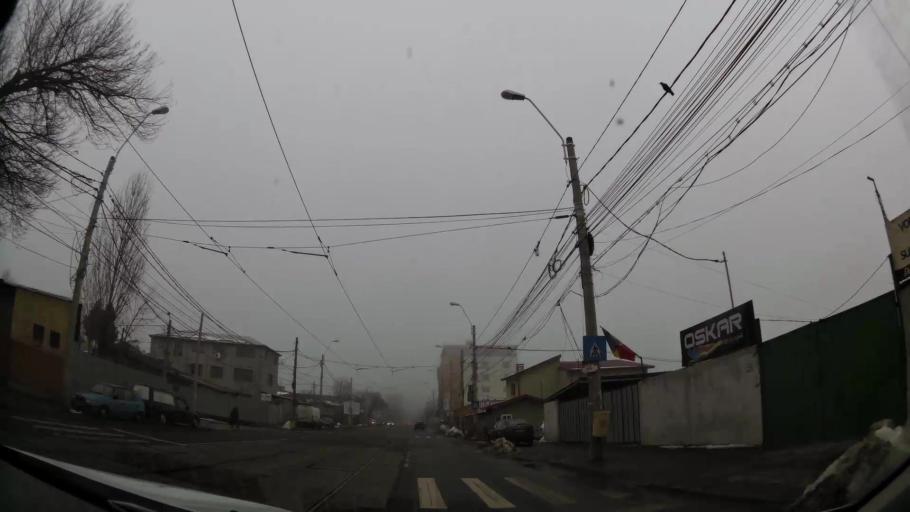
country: RO
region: Ilfov
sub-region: Comuna Chiajna
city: Rosu
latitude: 44.4650
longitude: 26.0385
